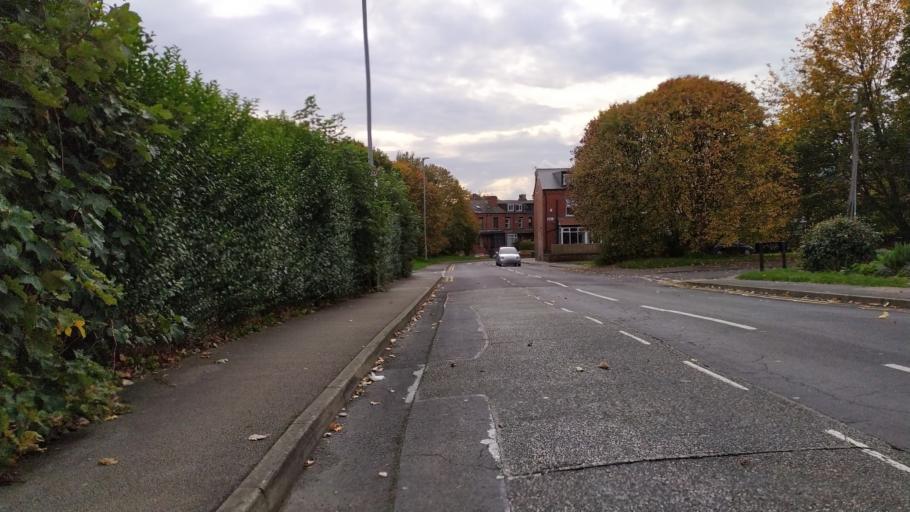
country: GB
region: England
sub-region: City and Borough of Leeds
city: Leeds
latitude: 53.8121
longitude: -1.5836
